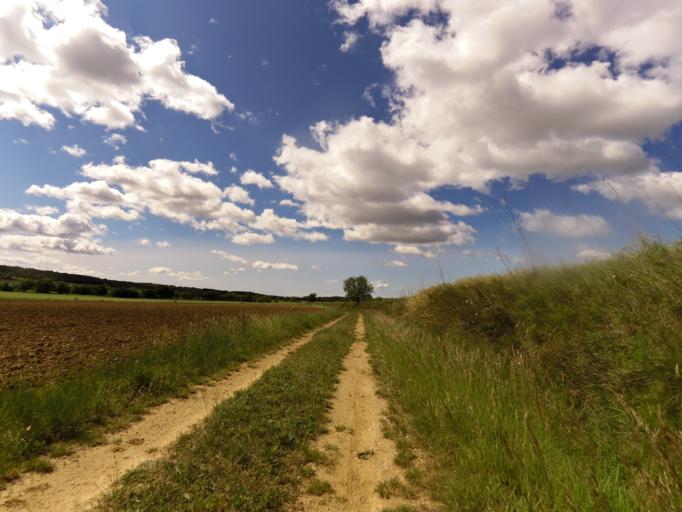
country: FR
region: Languedoc-Roussillon
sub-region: Departement du Gard
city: Calvisson
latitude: 43.7715
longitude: 4.2110
